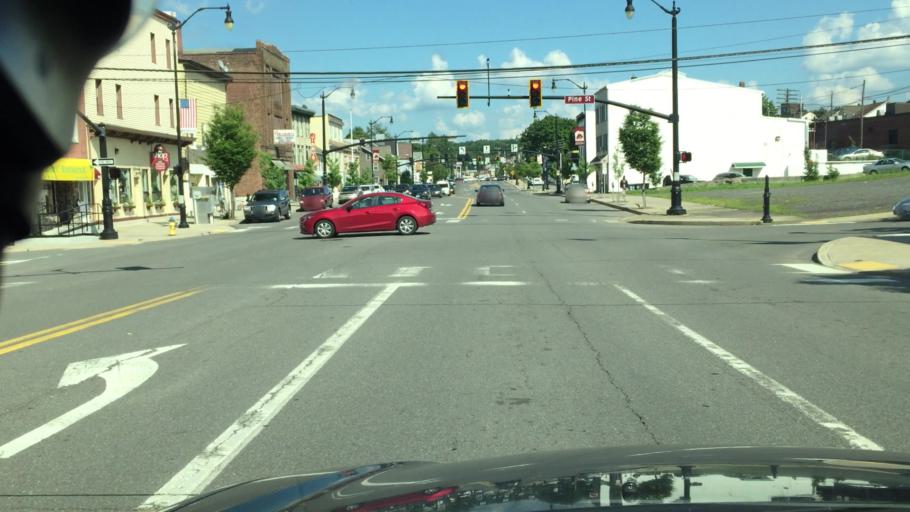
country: US
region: Pennsylvania
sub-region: Luzerne County
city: Hazleton
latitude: 40.9536
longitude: -75.9728
